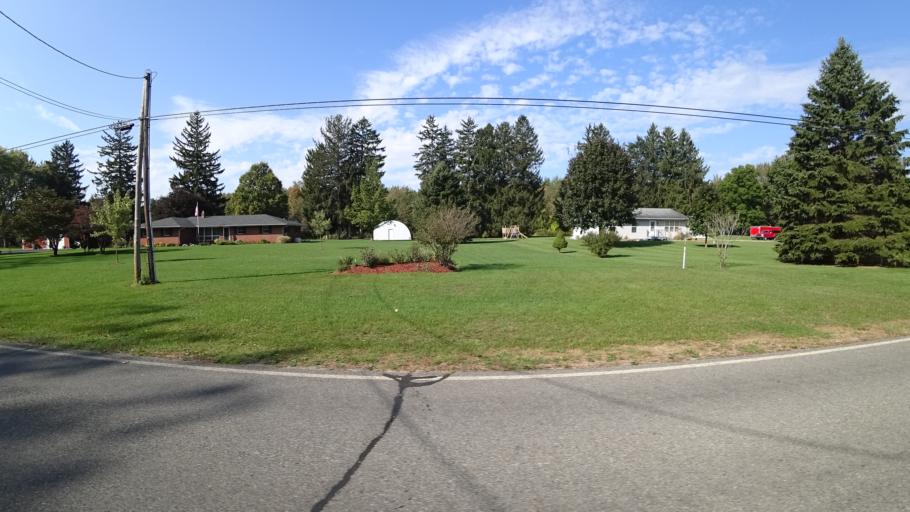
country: US
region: Michigan
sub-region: Saint Joseph County
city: Three Rivers
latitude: 41.9247
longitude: -85.6355
